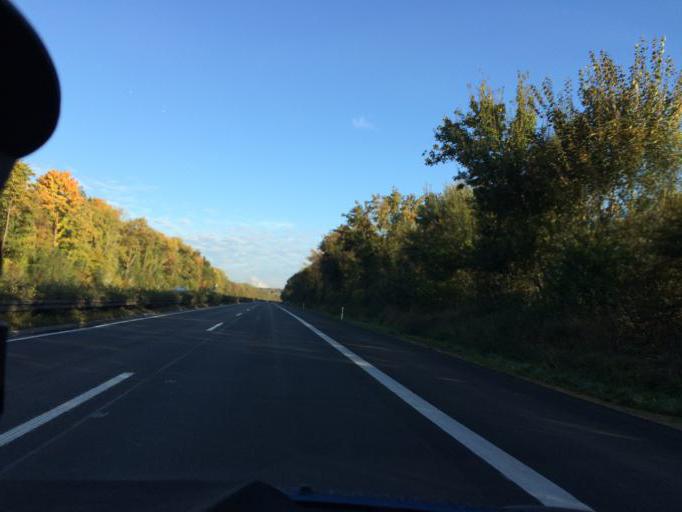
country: DE
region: North Rhine-Westphalia
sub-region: Regierungsbezirk Koln
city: Frechen
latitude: 50.8678
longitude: 6.8042
